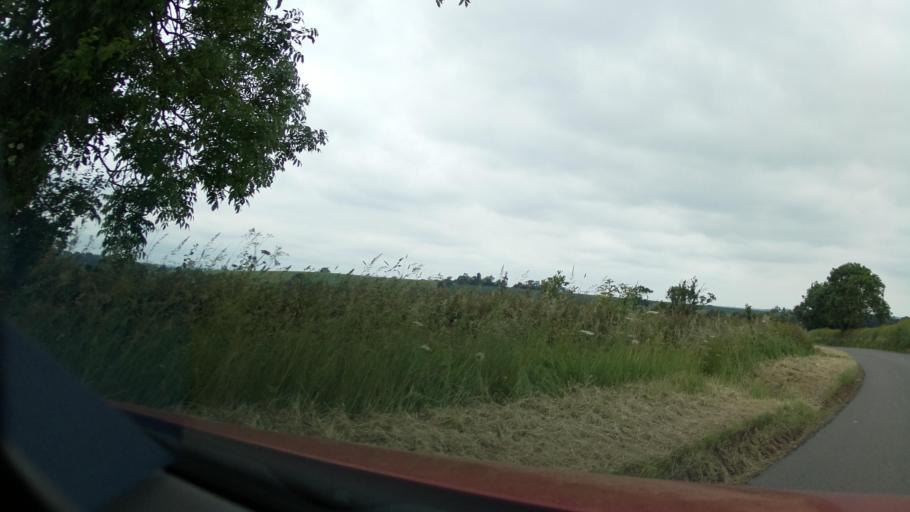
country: GB
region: England
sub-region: Leicestershire
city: Melton Mowbray
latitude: 52.7045
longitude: -0.8345
